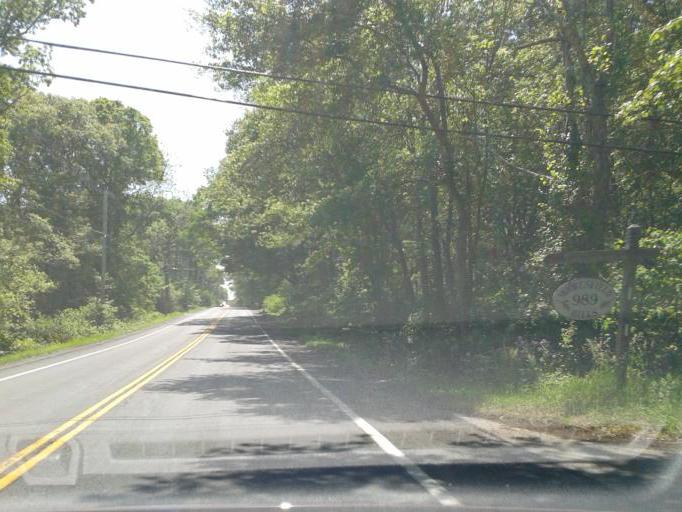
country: US
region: Rhode Island
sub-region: Washington County
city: Kingston
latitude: 41.4890
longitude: -71.4906
